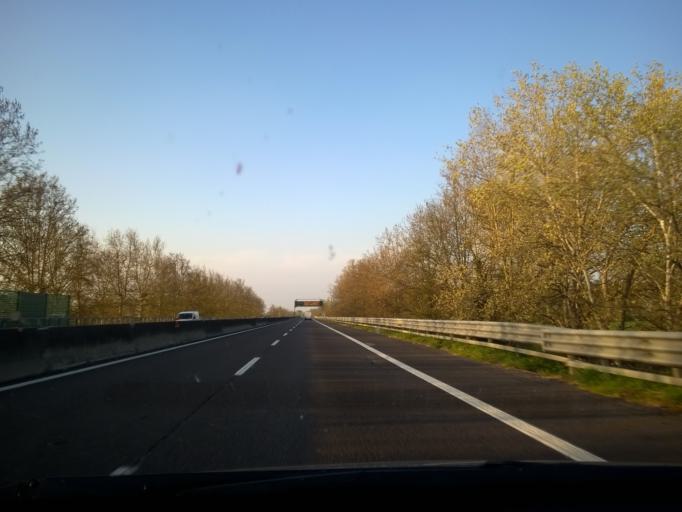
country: IT
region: Emilia-Romagna
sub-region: Provincia di Ferrara
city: Porotto-Cassama
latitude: 44.8510
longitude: 11.5674
